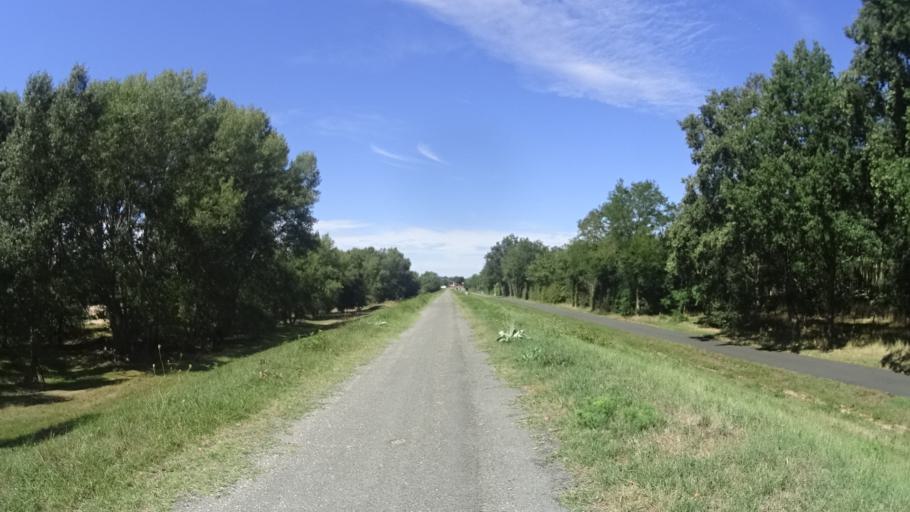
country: FR
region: Centre
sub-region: Departement du Loiret
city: Briare
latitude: 47.5954
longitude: 2.7690
